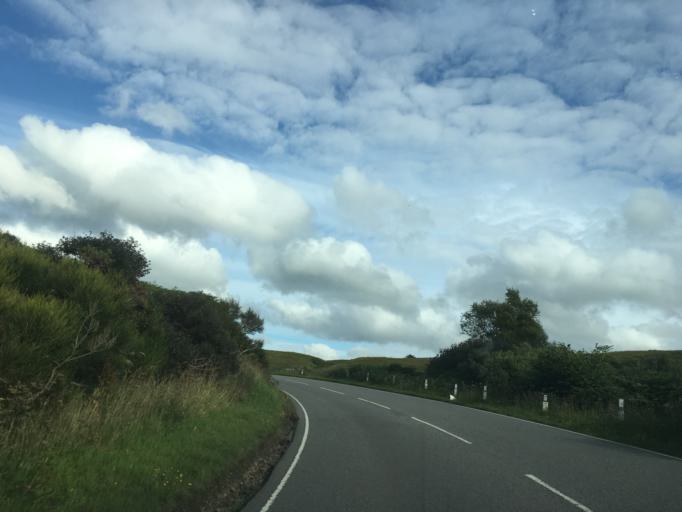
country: GB
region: Scotland
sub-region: Argyll and Bute
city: Oban
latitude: 56.3935
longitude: -5.4685
